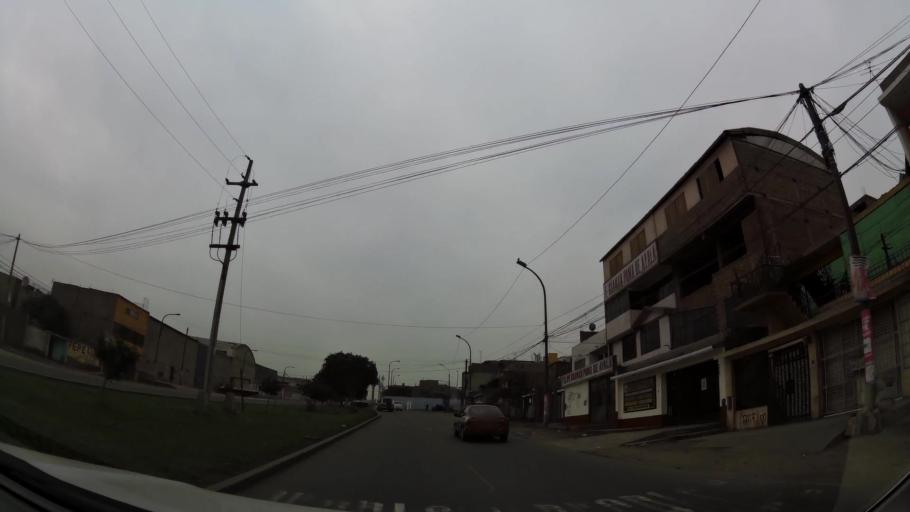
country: PE
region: Lima
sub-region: Lima
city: Independencia
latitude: -11.9843
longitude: -76.9941
